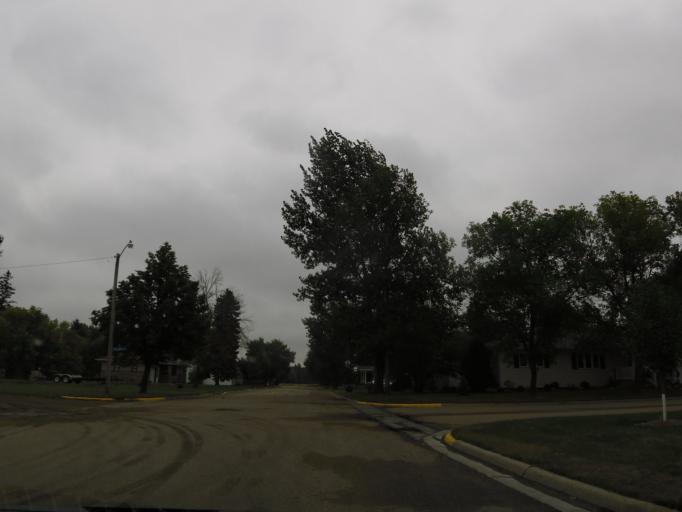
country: US
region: Minnesota
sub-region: Marshall County
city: Warren
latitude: 48.3342
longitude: -96.8145
